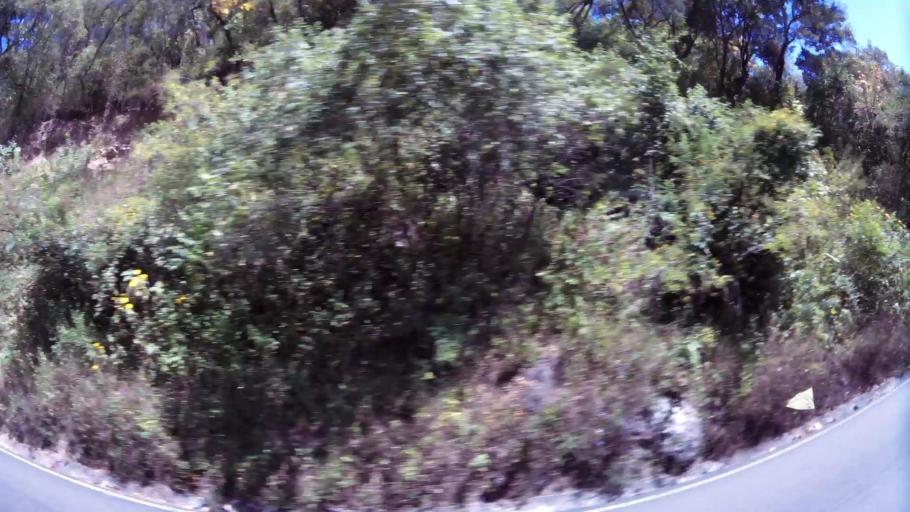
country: GT
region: Solola
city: Panajachel
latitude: 14.7436
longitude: -91.1623
